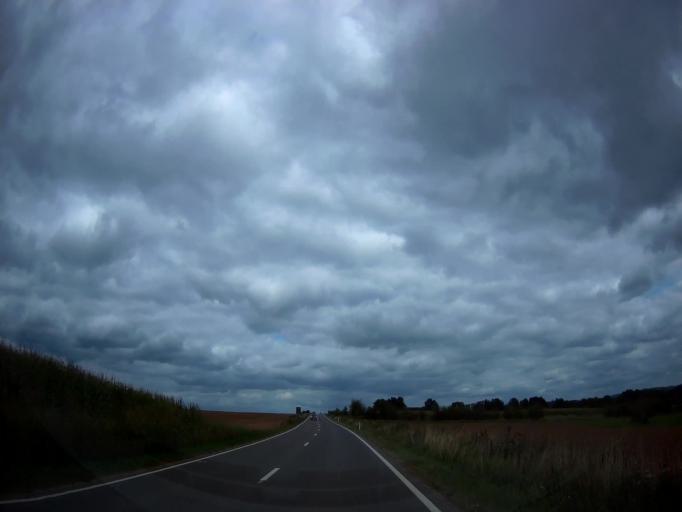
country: BE
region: Wallonia
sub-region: Province de Namur
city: Rochefort
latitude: 50.1795
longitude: 5.2832
